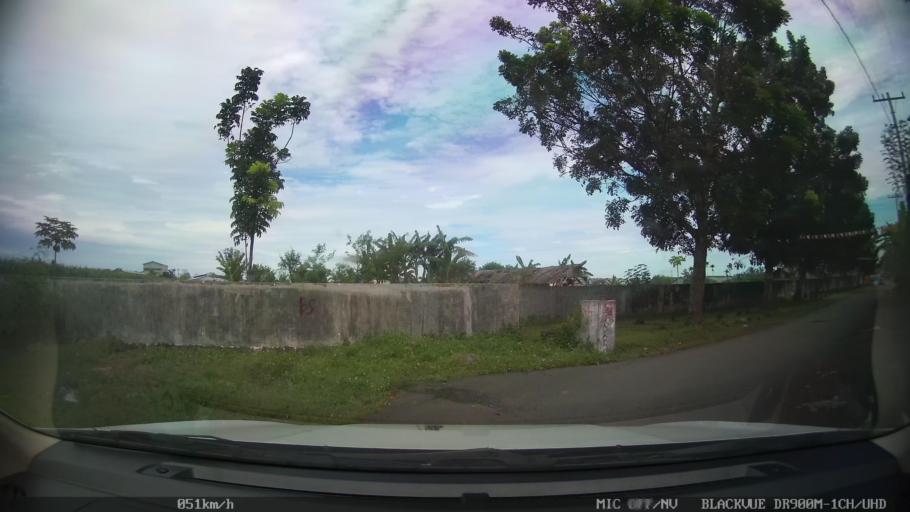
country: ID
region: North Sumatra
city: Sunggal
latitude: 3.5865
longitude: 98.5799
